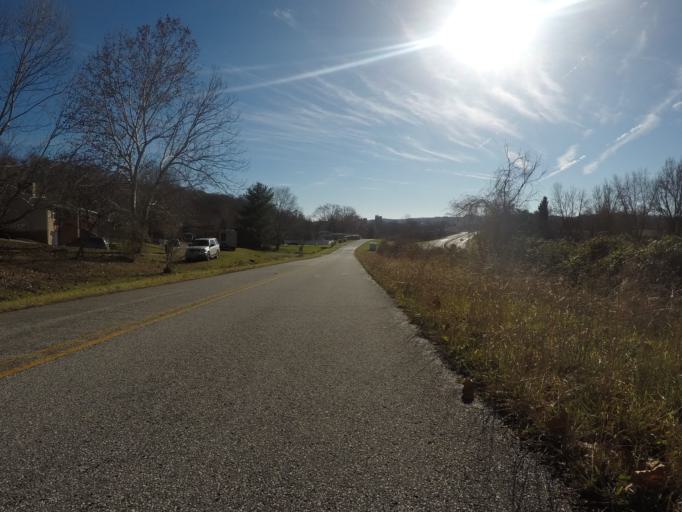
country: US
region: West Virginia
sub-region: Cabell County
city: Huntington
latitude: 38.4335
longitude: -82.4551
